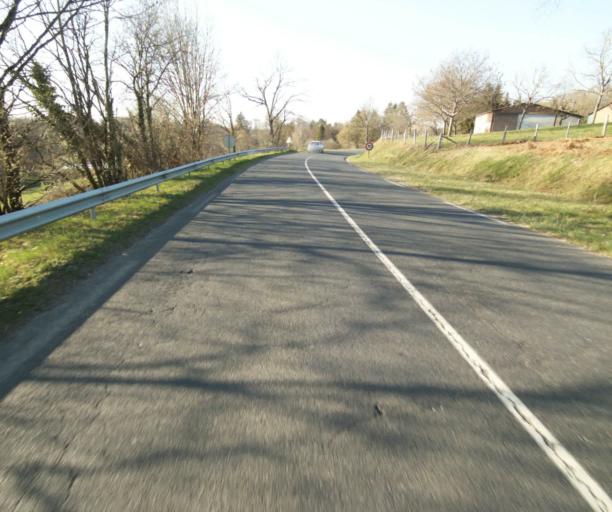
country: FR
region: Limousin
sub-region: Departement de la Correze
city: Saint-Clement
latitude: 45.3194
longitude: 1.6790
